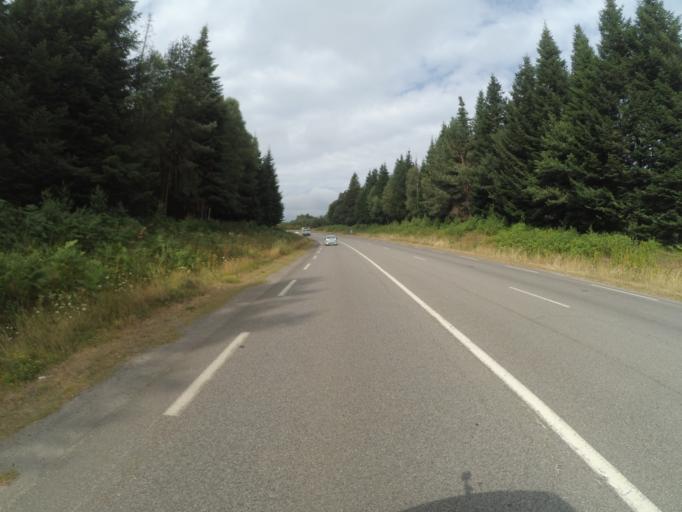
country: FR
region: Limousin
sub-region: Departement de la Correze
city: Ussel
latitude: 45.5179
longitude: 2.2647
